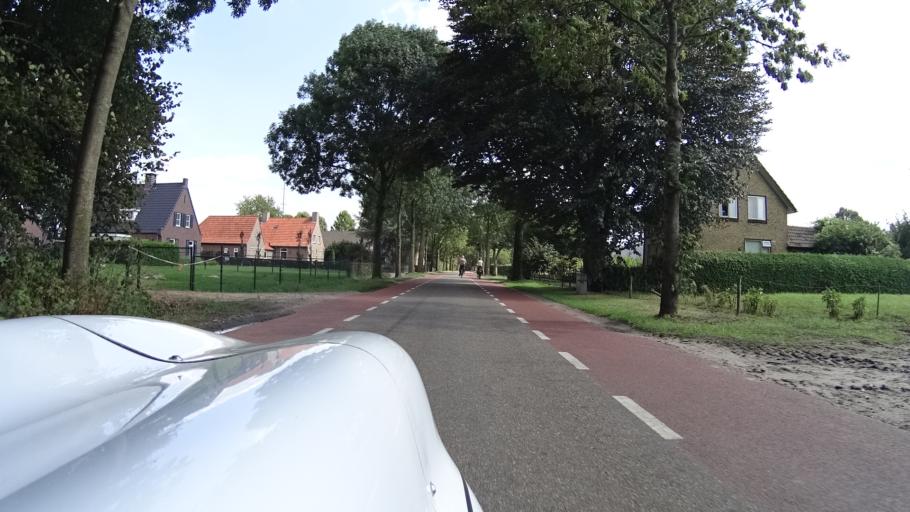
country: NL
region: North Brabant
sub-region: Gemeente Veghel
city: Mariaheide
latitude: 51.6358
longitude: 5.5993
